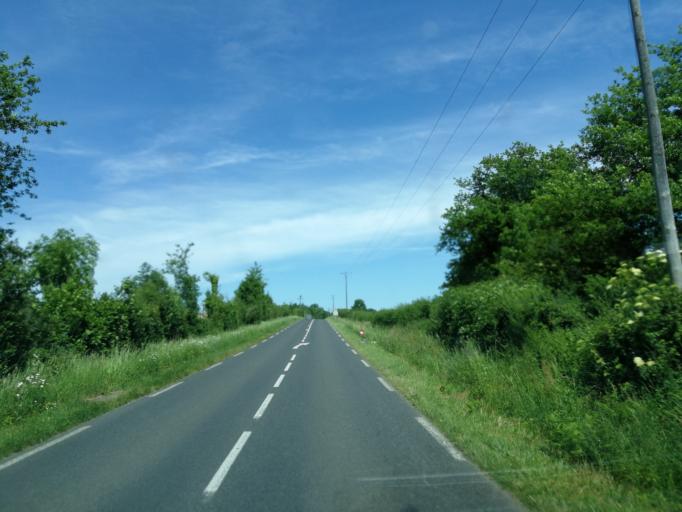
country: FR
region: Poitou-Charentes
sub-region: Departement des Deux-Sevres
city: Courlay
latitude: 46.8179
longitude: -0.5317
